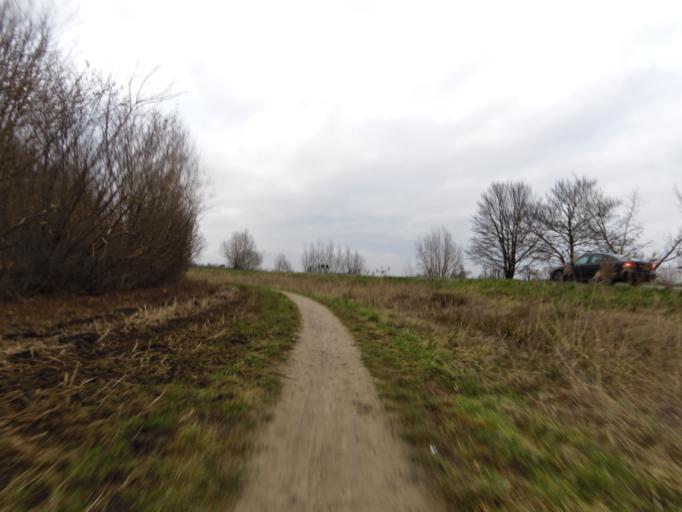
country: GB
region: England
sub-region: Cambridgeshire
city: Waterbeach
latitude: 52.2603
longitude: 0.1991
